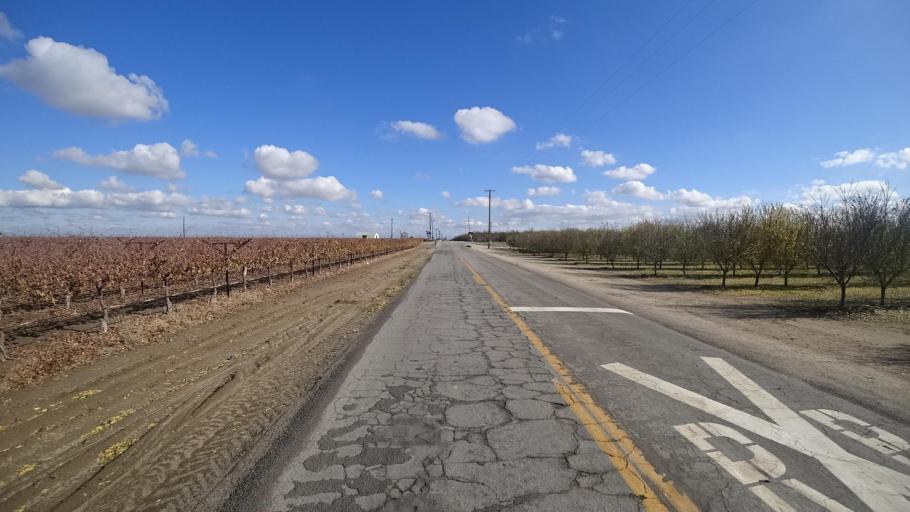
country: US
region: California
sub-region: Kern County
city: Delano
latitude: 35.7322
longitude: -119.3367
